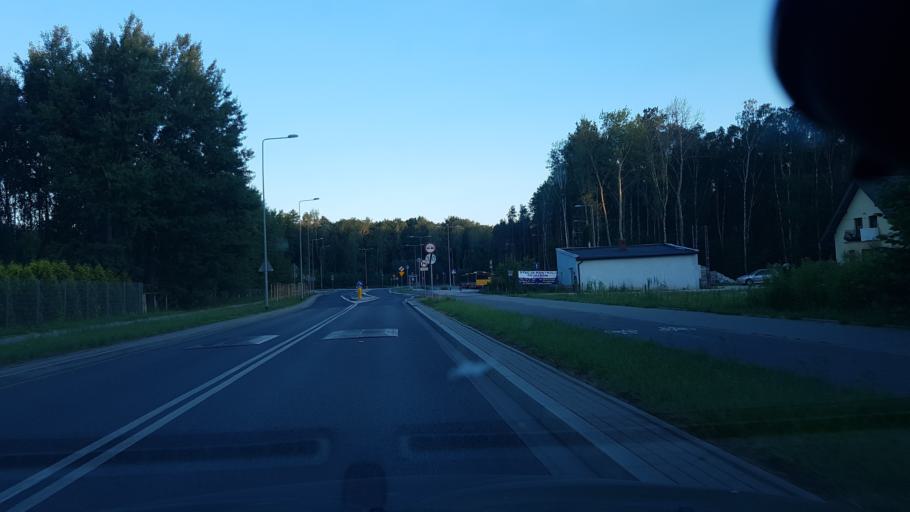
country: PL
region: Masovian Voivodeship
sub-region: Warszawa
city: Wesola
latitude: 52.2160
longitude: 21.2181
